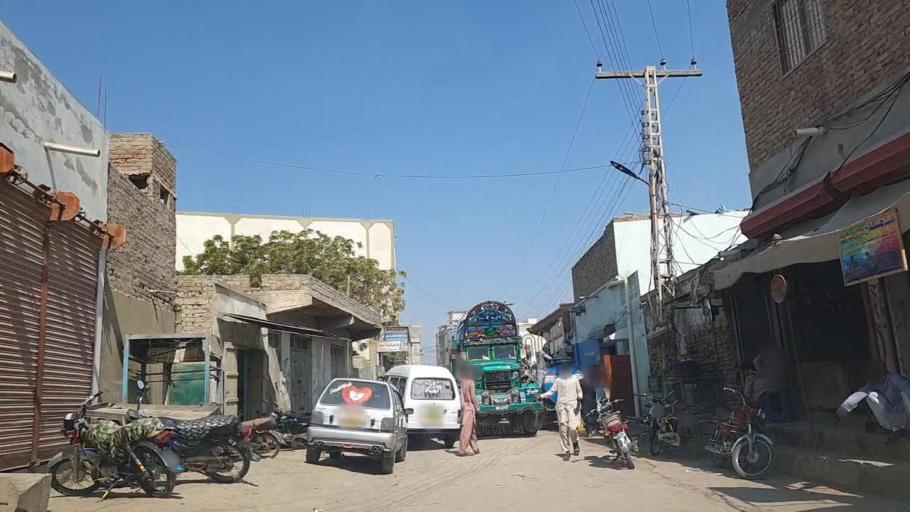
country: PK
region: Sindh
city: Naukot
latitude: 24.8558
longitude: 69.4028
